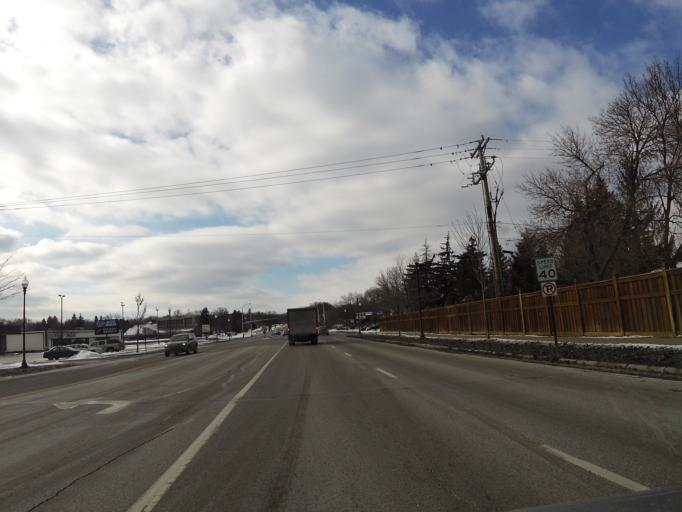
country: US
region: Minnesota
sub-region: Hennepin County
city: Minnetonka Mills
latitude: 44.9209
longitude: -93.4247
